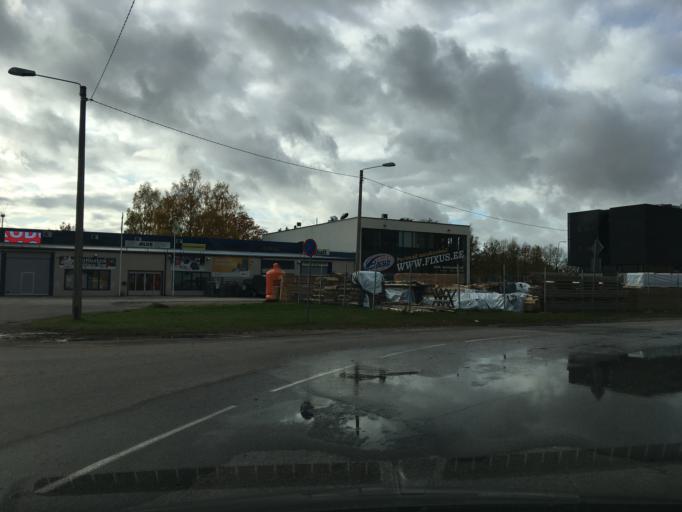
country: EE
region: Paernumaa
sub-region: Paernu linn
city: Parnu
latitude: 58.3732
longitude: 24.5455
